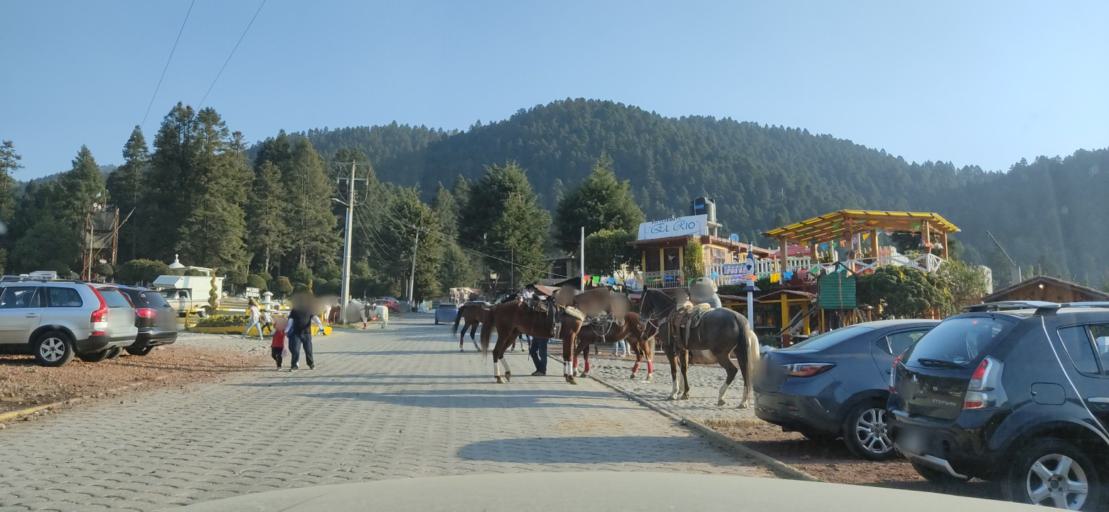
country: MX
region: Mexico
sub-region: Ocoyoacac
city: San Jeronimo Acazulco
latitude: 19.2442
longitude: -99.3770
